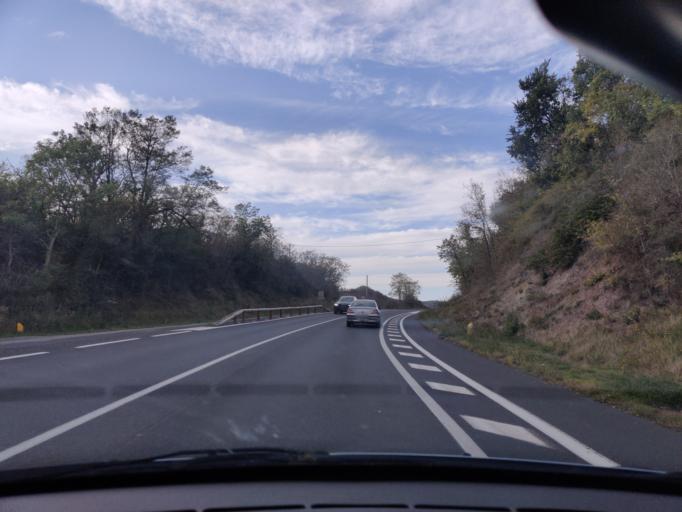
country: FR
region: Auvergne
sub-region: Departement du Puy-de-Dome
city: Mozac
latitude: 45.9078
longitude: 3.0864
